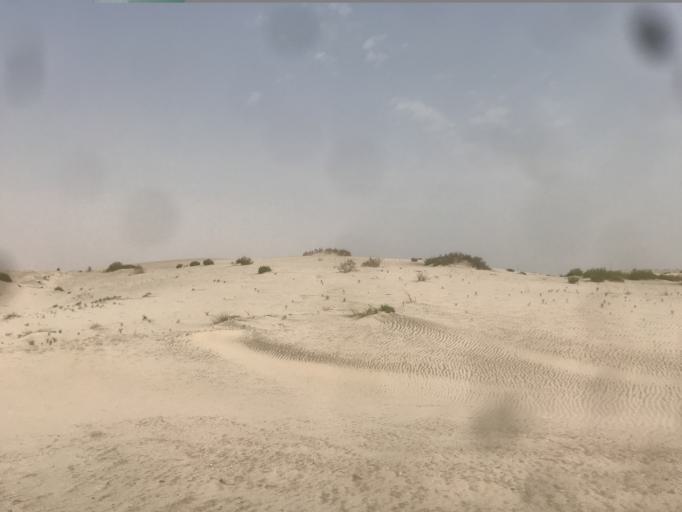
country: SA
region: Eastern Province
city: Abqaiq
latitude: 25.9072
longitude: 49.9970
